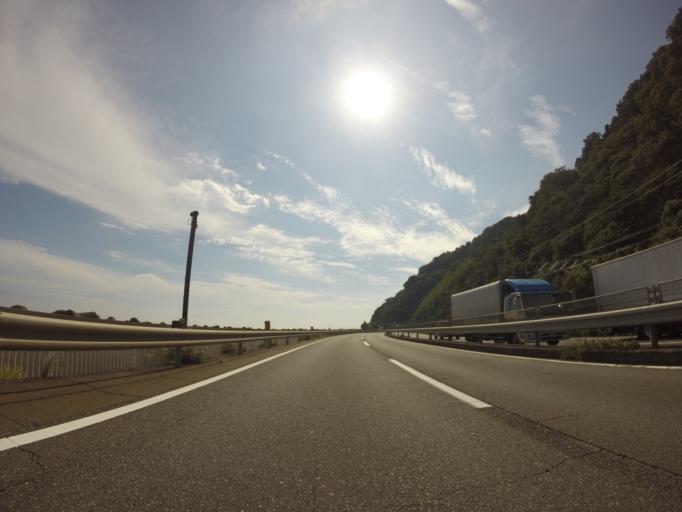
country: JP
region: Shizuoka
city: Fujinomiya
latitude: 35.0695
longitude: 138.5424
